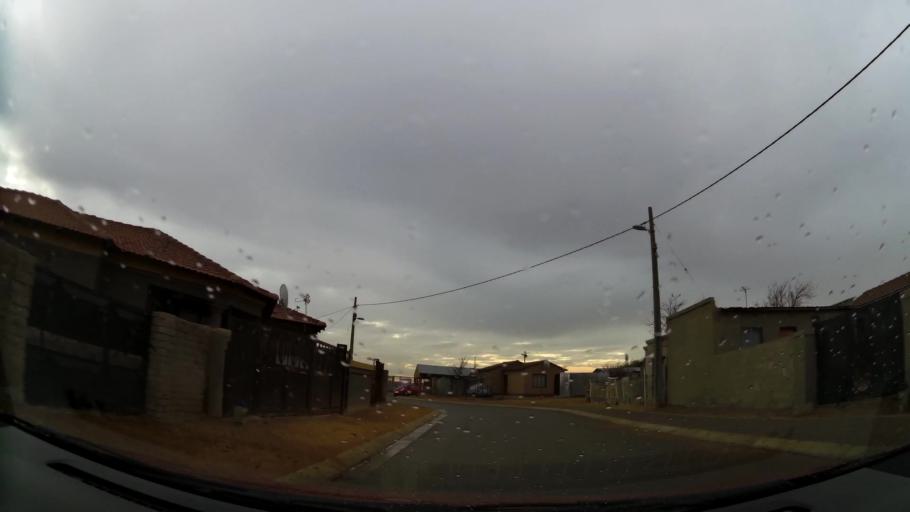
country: ZA
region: Gauteng
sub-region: City of Johannesburg Metropolitan Municipality
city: Roodepoort
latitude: -26.1761
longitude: 27.7896
